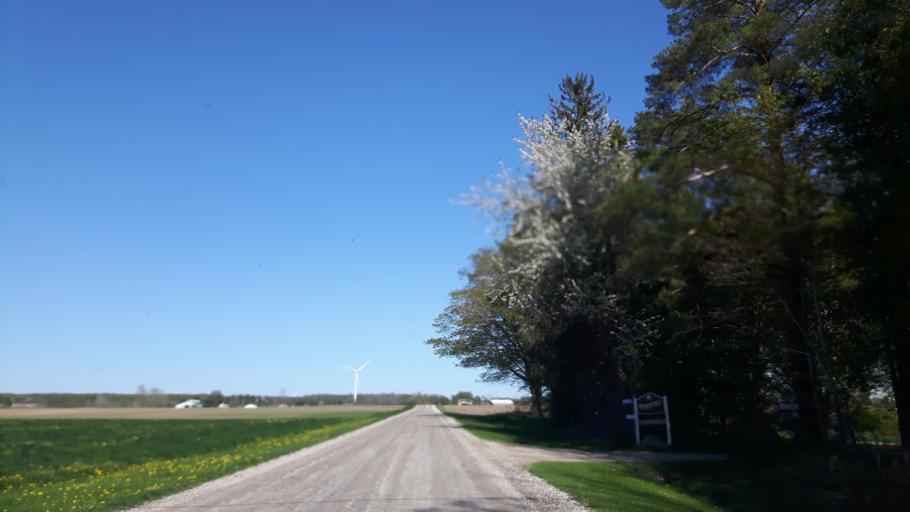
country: CA
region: Ontario
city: Bluewater
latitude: 43.5092
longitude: -81.6820
